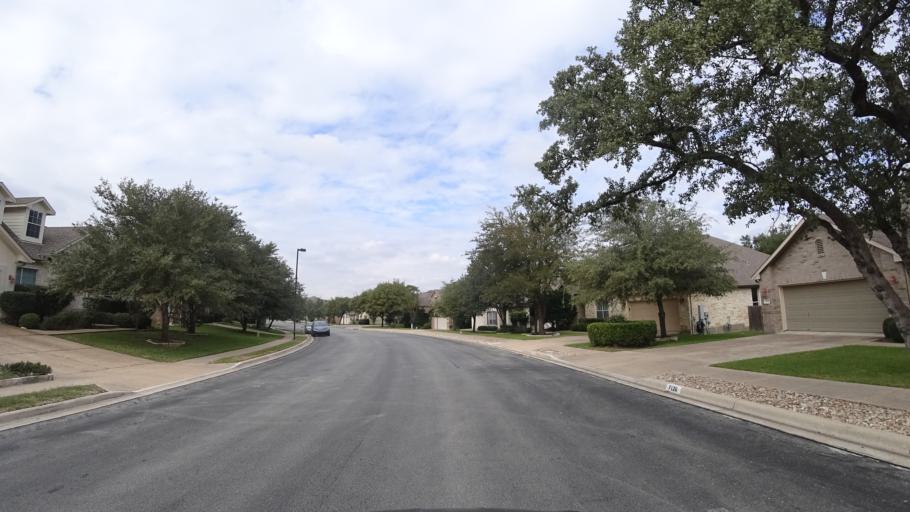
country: US
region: Texas
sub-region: Travis County
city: Shady Hollow
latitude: 30.1898
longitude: -97.9013
